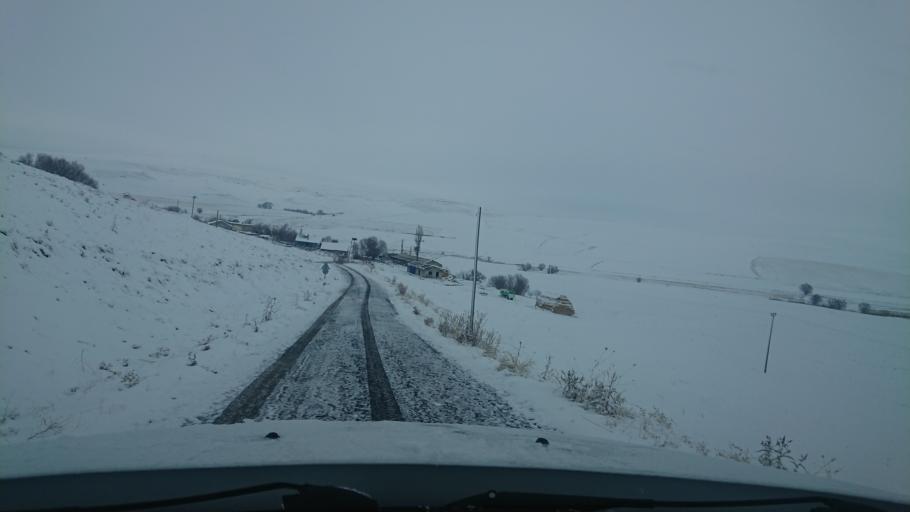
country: TR
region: Aksaray
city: Acipinar
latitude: 38.6740
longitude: 33.8647
